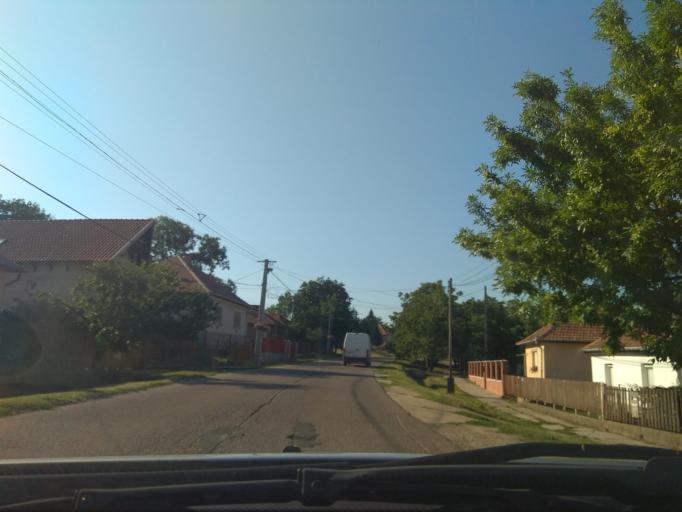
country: HU
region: Borsod-Abauj-Zemplen
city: Emod
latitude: 47.9382
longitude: 20.8169
